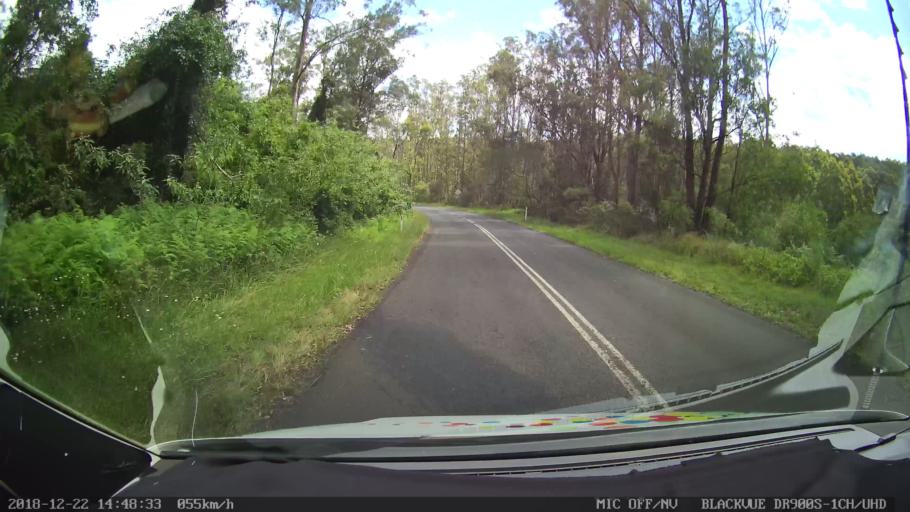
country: AU
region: New South Wales
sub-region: Bellingen
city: Dorrigo
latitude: -30.1815
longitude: 152.5520
